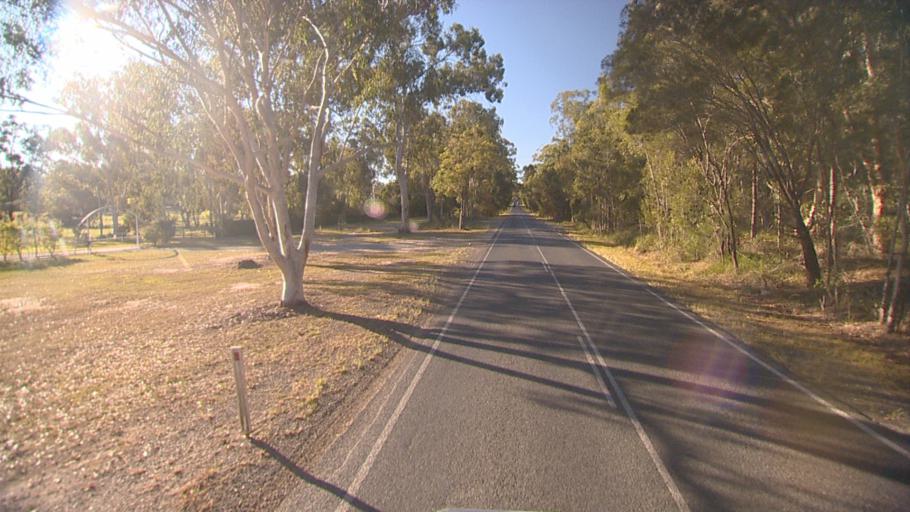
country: AU
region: Queensland
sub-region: Logan
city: Logan Reserve
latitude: -27.7317
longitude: 153.0890
